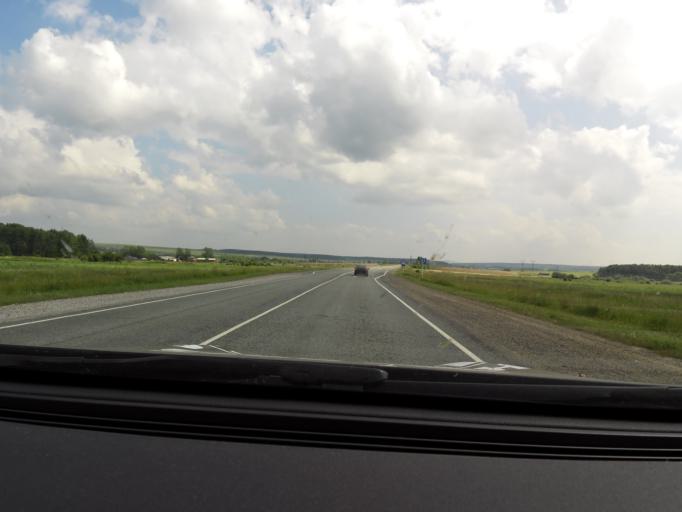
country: RU
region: Sverdlovsk
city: Achit
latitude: 56.7937
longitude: 57.8741
